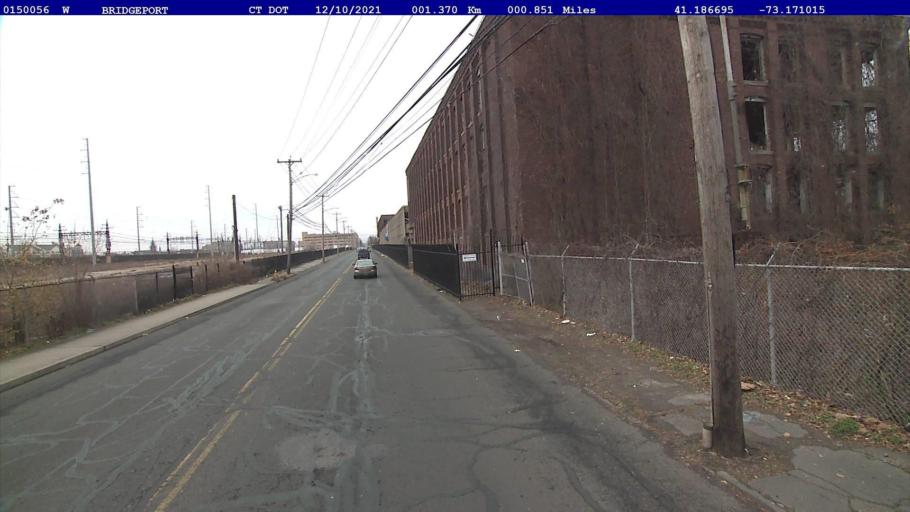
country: US
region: Connecticut
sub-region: Fairfield County
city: Stratford
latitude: 41.1867
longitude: -73.1710
